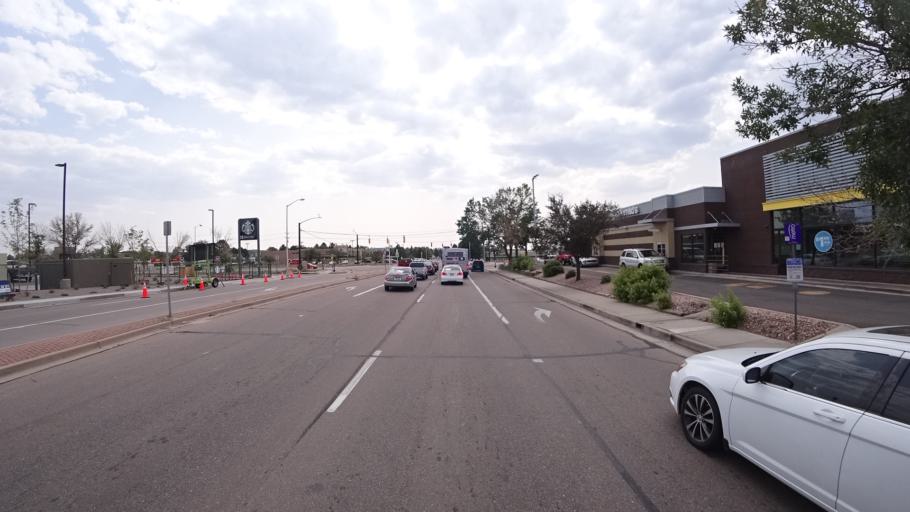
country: US
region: Colorado
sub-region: El Paso County
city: Cimarron Hills
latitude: 38.8406
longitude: -104.7482
